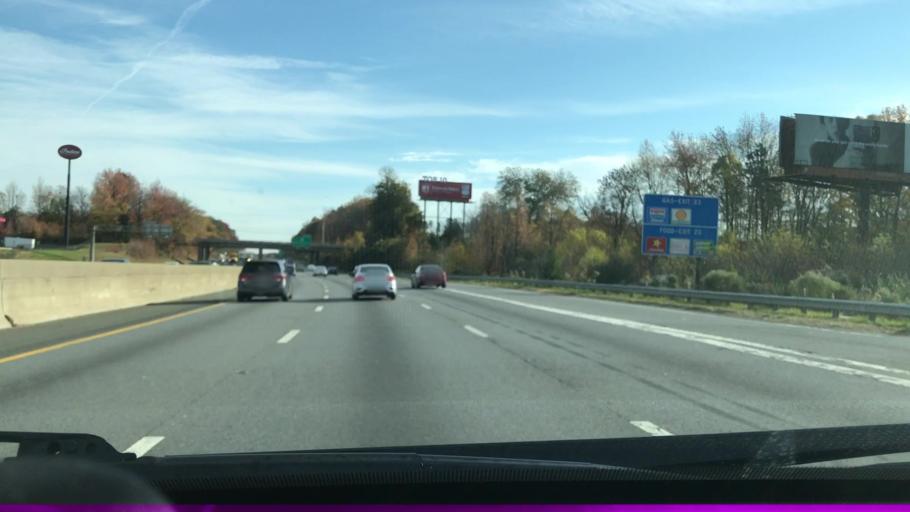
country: US
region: North Carolina
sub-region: Gaston County
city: Lowell
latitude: 35.2602
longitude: -81.1016
